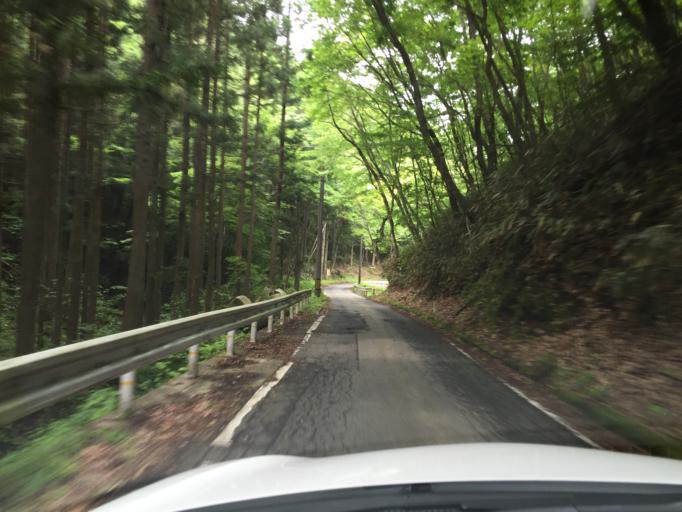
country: JP
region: Fukushima
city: Iwaki
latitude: 37.2049
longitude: 140.7223
